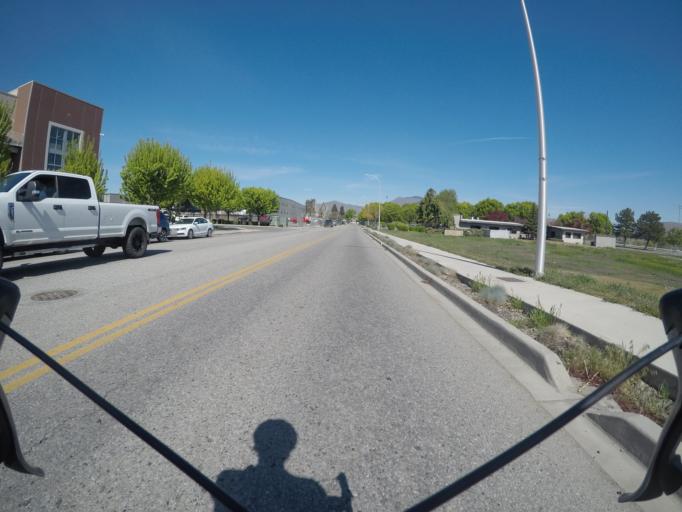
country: US
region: Washington
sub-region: Chelan County
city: Wenatchee
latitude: 47.4432
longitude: -120.3208
